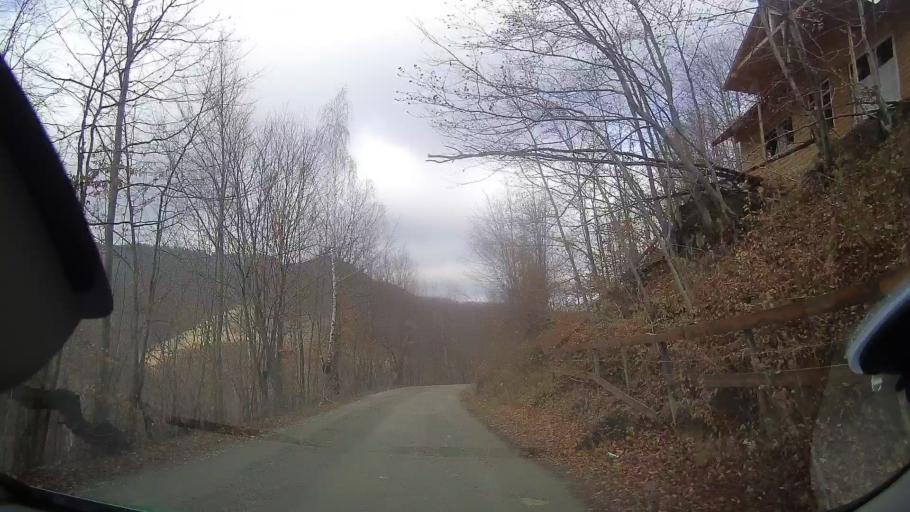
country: RO
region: Cluj
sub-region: Comuna Valea Ierii
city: Valea Ierii
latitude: 46.6851
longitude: 23.3095
